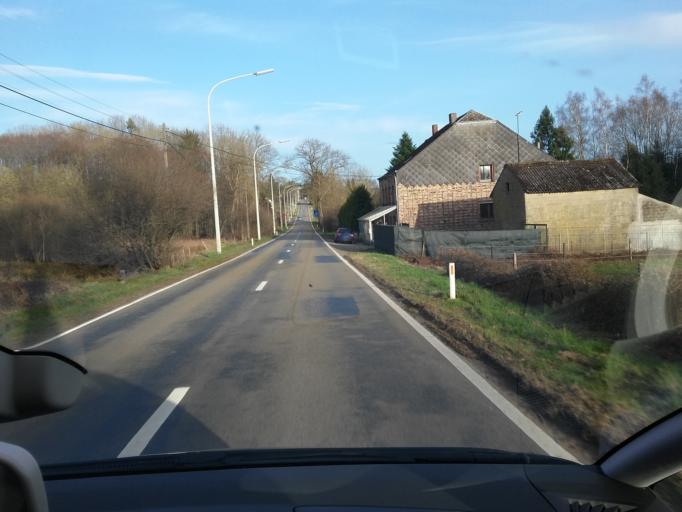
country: BE
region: Wallonia
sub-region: Province du Luxembourg
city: Libin
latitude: 50.0099
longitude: 5.2063
